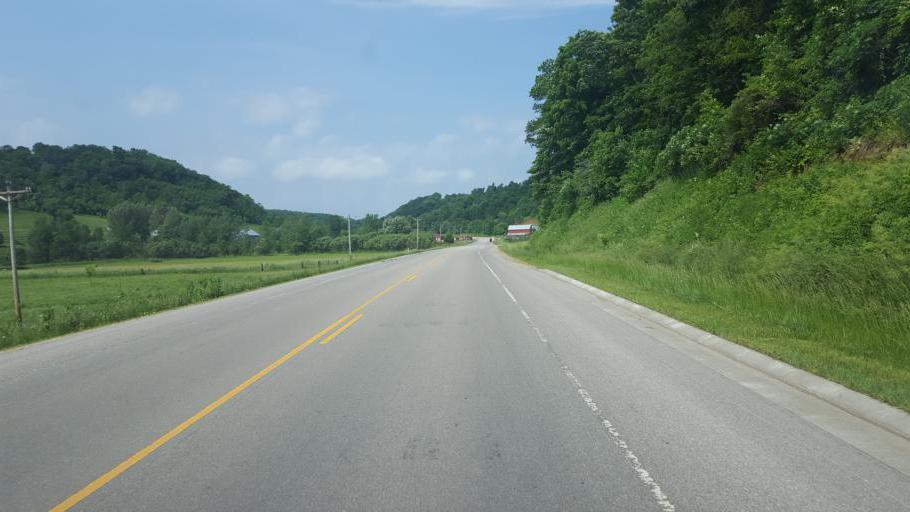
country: US
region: Wisconsin
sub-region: Monroe County
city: Cashton
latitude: 43.7344
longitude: -90.7043
